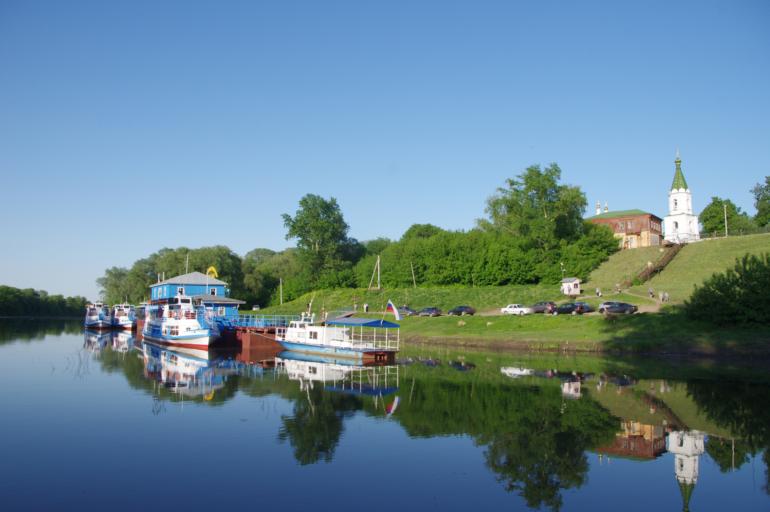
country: RU
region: Rjazan
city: Ryazan'
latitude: 54.6378
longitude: 39.7479
